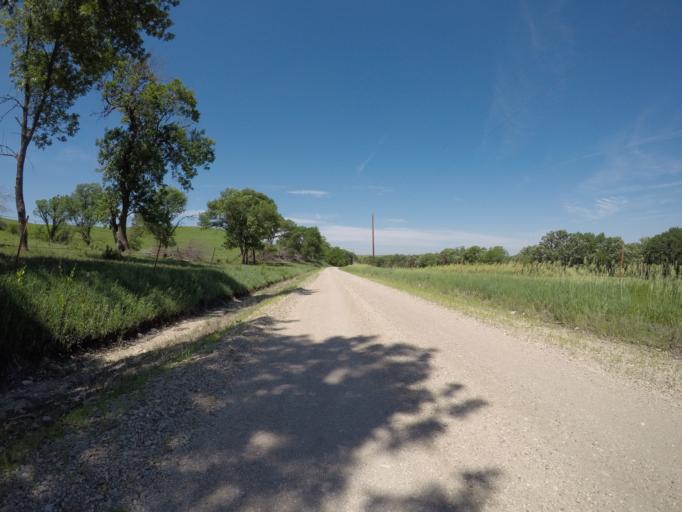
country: US
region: Kansas
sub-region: Wabaunsee County
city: Alma
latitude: 39.0007
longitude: -96.1999
